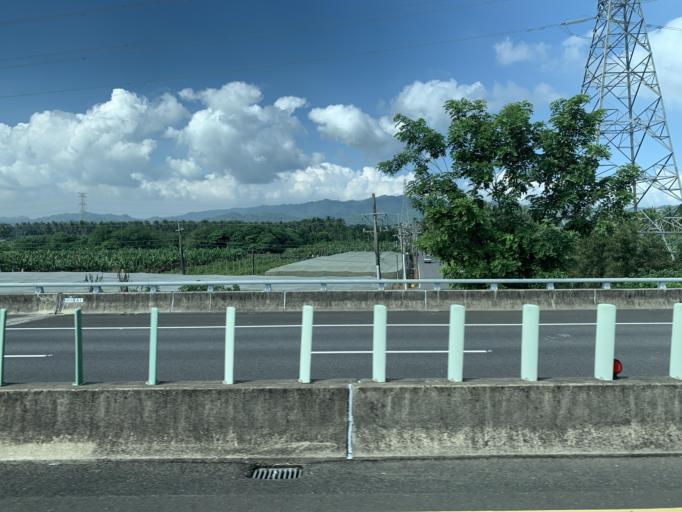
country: TW
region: Taiwan
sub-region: Pingtung
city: Pingtung
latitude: 22.8456
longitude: 120.4957
